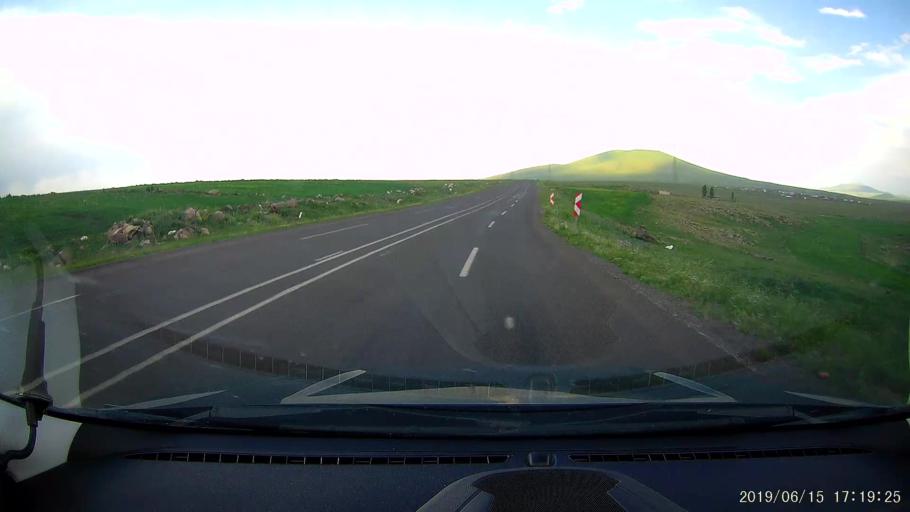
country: TR
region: Kars
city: Kars
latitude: 40.6167
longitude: 43.2779
